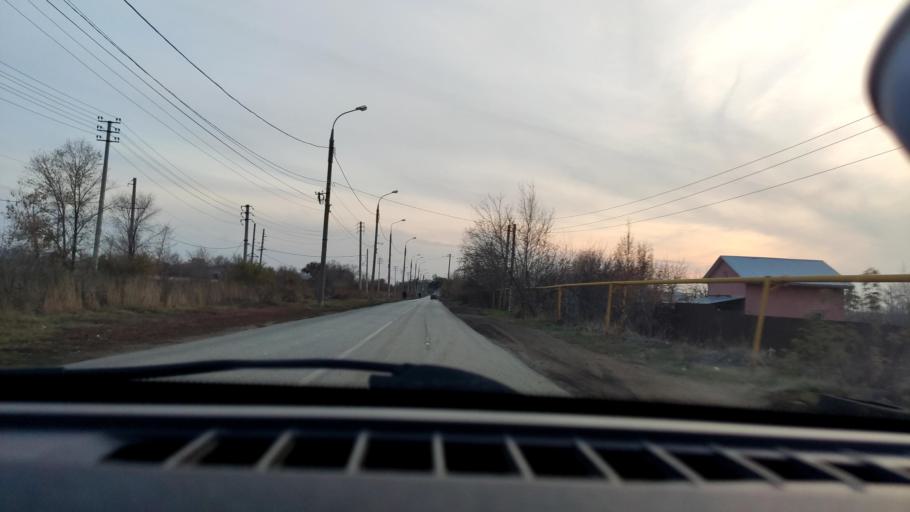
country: RU
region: Samara
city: Samara
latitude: 53.1474
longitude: 50.1348
